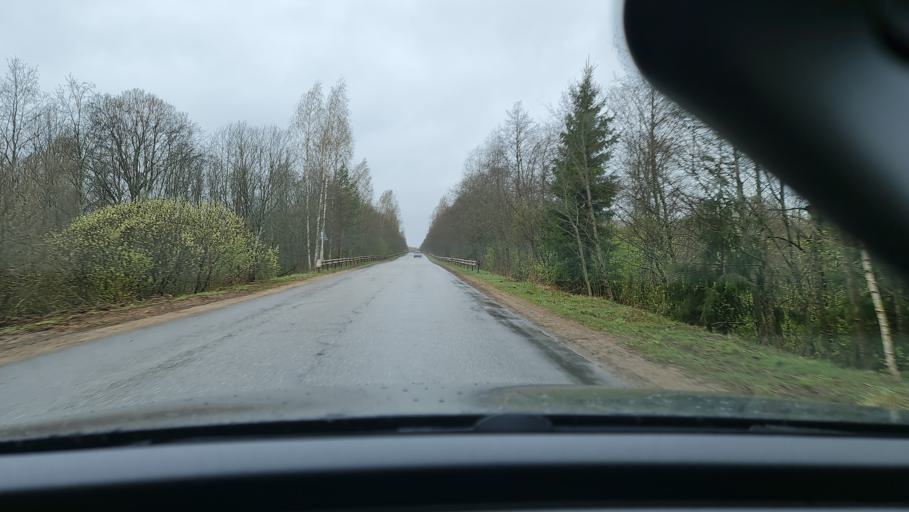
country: RU
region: Novgorod
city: Kresttsy
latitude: 57.9720
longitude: 32.7239
